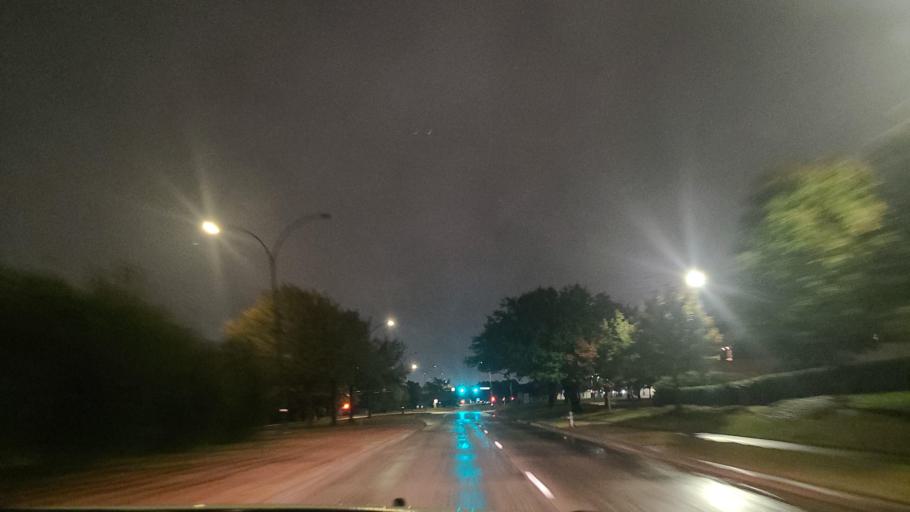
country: US
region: Texas
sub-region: Tarrant County
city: Dalworthington Gardens
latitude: 32.6827
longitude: -97.1199
